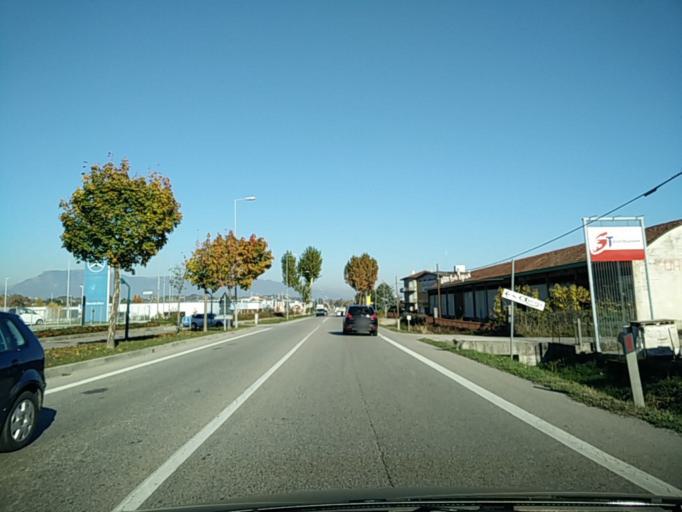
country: IT
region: Veneto
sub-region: Provincia di Treviso
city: Susegana
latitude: 45.8569
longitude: 12.2591
